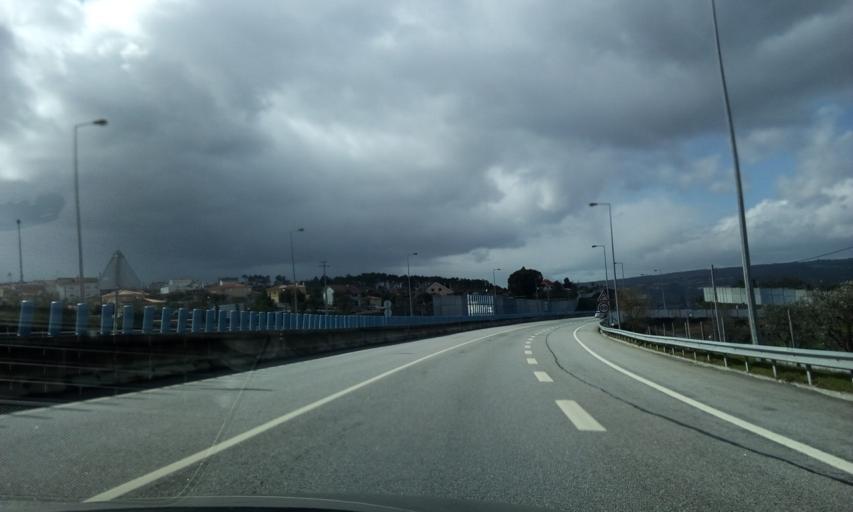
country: PT
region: Viseu
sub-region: Mangualde
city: Mangualde
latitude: 40.6279
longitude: -7.8004
